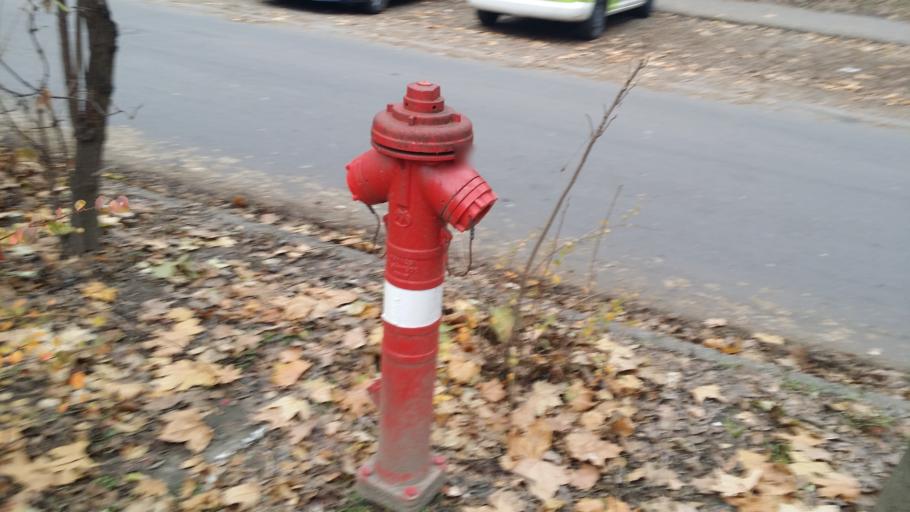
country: HU
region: Pest
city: Budakalasz
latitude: 47.6019
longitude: 19.0600
